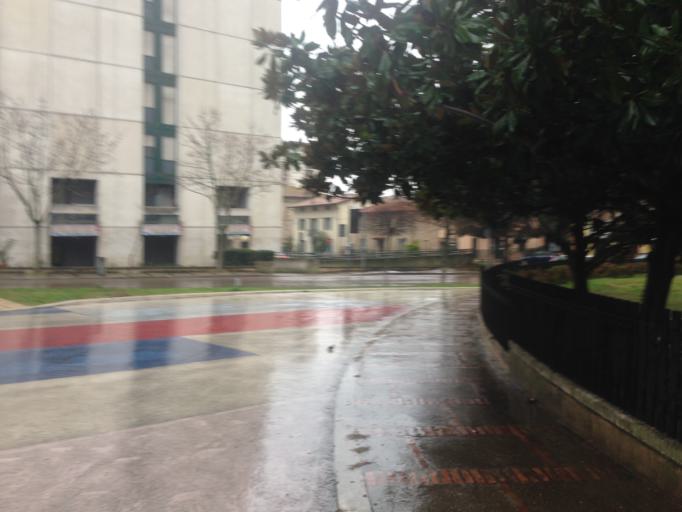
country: IT
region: Umbria
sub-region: Provincia di Perugia
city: Perugia
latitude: 43.1045
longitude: 12.3740
